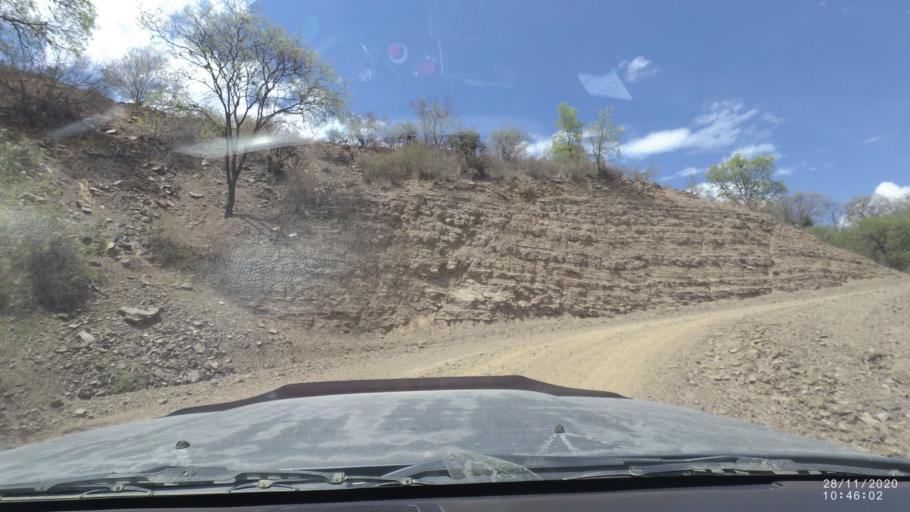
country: BO
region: Cochabamba
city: Capinota
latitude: -17.7875
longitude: -66.1278
